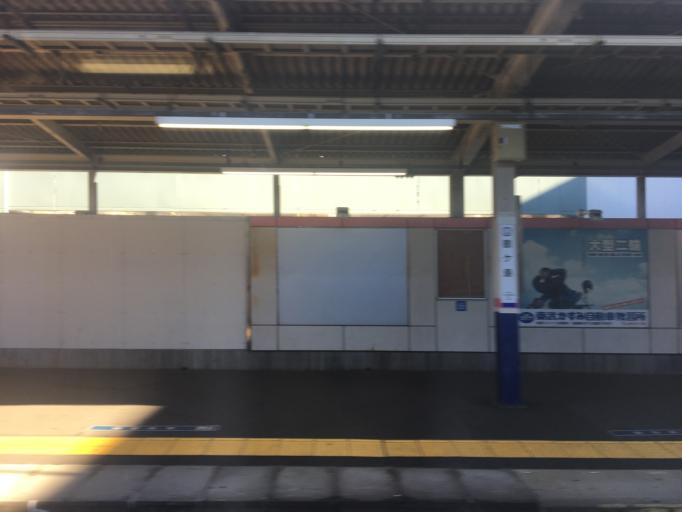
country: JP
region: Saitama
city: Sakado
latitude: 35.9370
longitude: 139.4236
